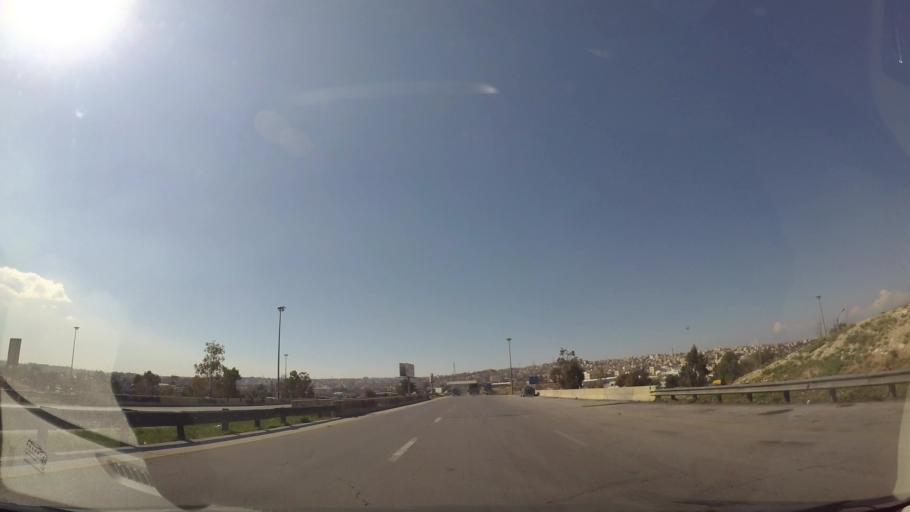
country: JO
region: Zarqa
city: Russeifa
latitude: 32.0285
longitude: 36.0893
